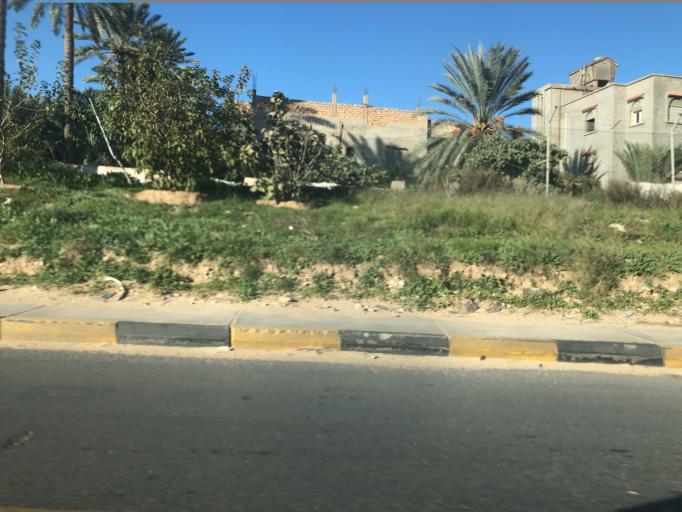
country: LY
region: Tripoli
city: Tripoli
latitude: 32.8688
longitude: 13.2530
